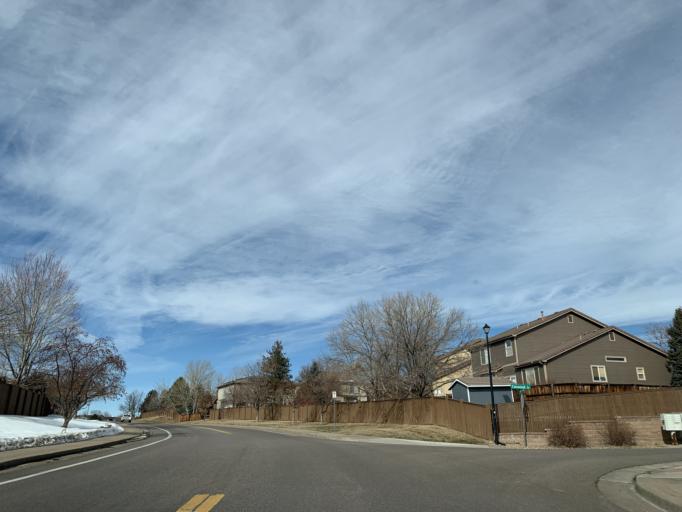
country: US
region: Colorado
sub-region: Douglas County
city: Carriage Club
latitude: 39.5318
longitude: -104.9357
